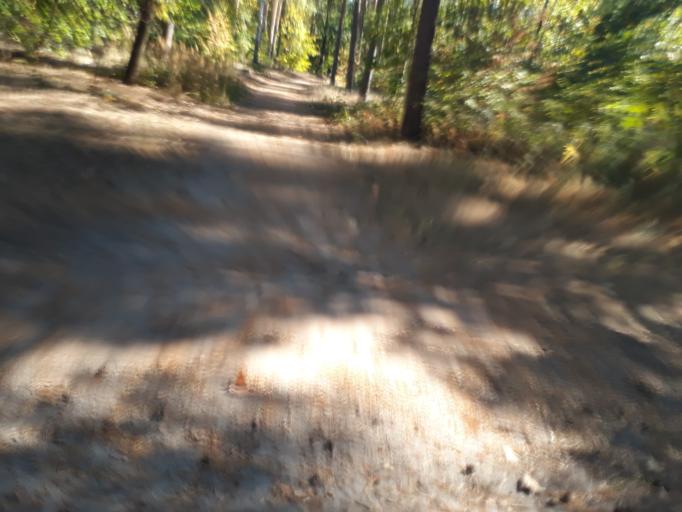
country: DE
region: Berlin
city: Grunewald
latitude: 52.4952
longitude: 13.2514
